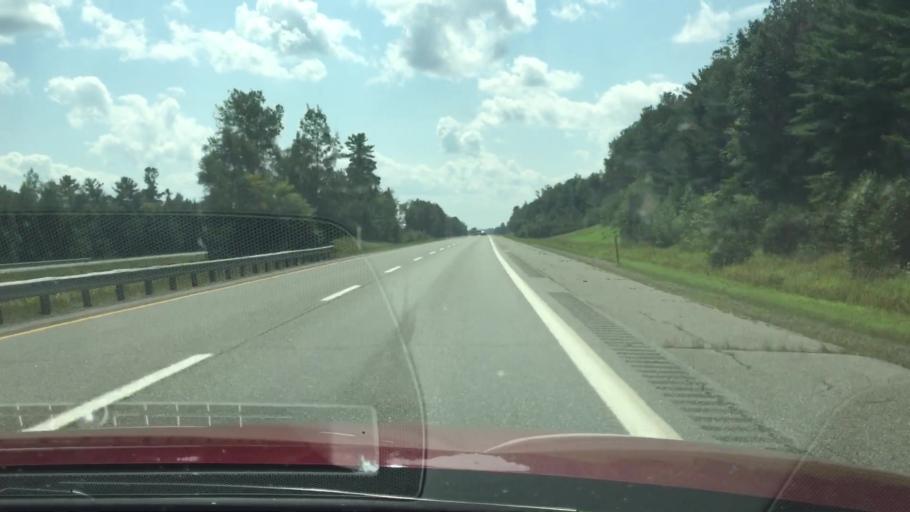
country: US
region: Maine
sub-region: Penobscot County
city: Medway
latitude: 45.5015
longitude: -68.5584
